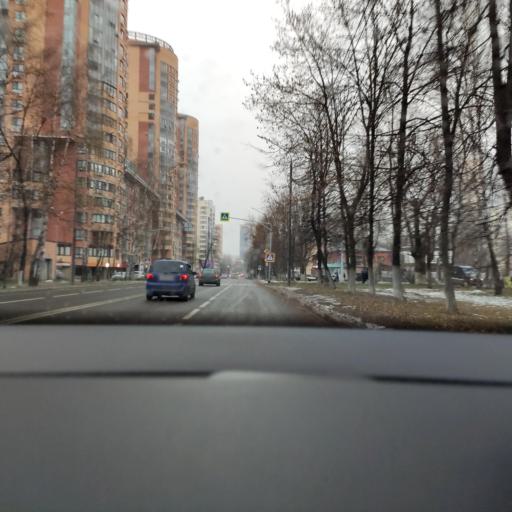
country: RU
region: Moskovskaya
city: Reutov
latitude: 55.7542
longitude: 37.8585
